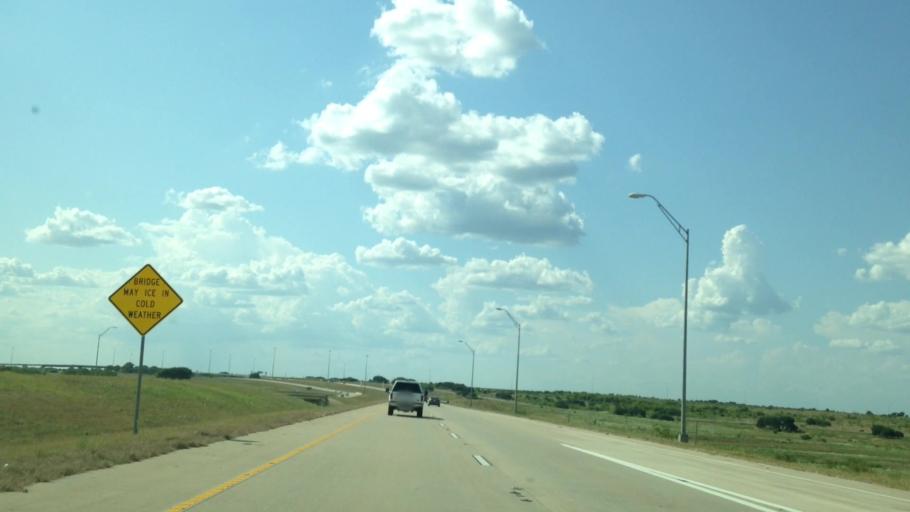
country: US
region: Texas
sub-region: Travis County
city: Onion Creek
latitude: 30.1051
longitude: -97.7865
